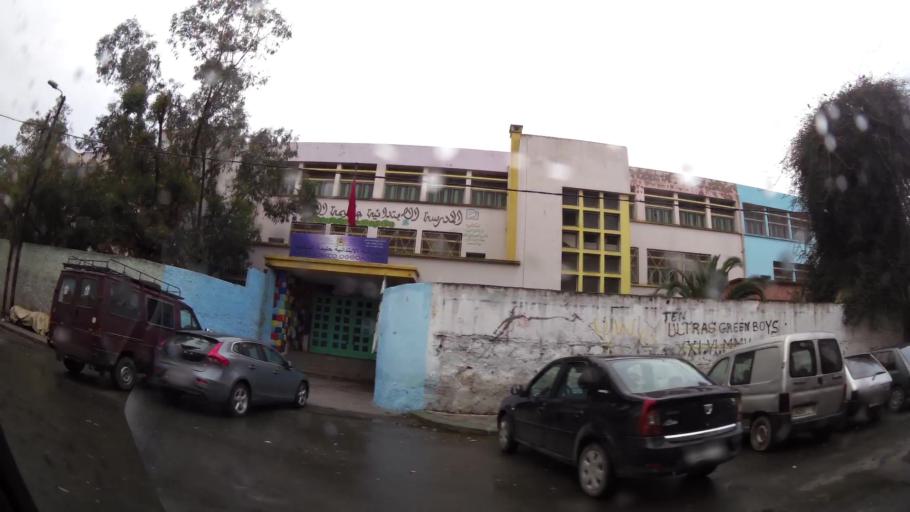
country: MA
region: Grand Casablanca
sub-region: Casablanca
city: Casablanca
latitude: 33.5538
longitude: -7.5736
